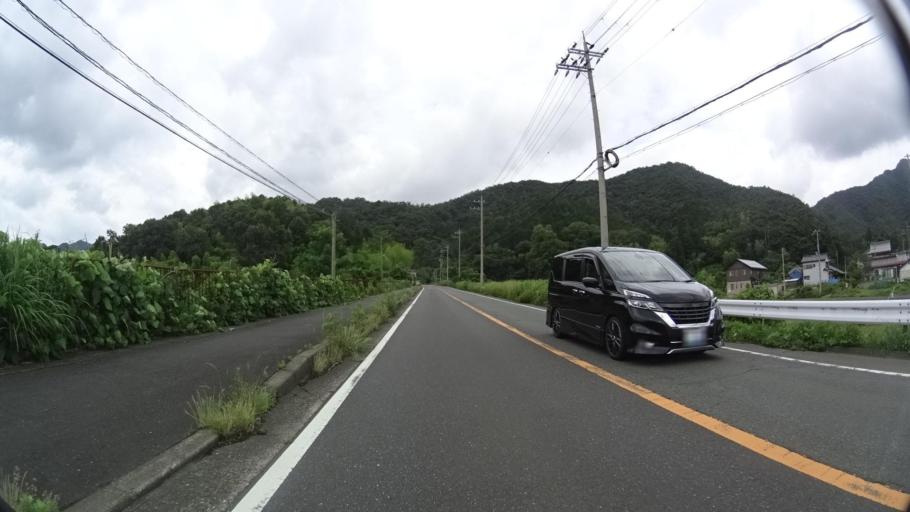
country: JP
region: Kyoto
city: Maizuru
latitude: 35.4967
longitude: 135.3913
